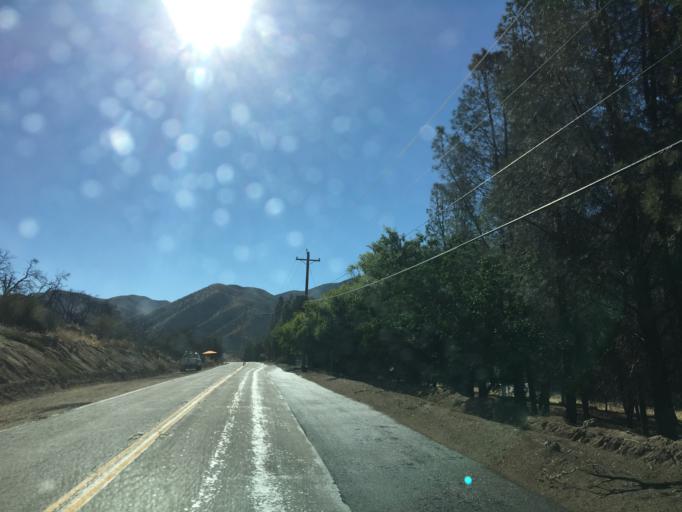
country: US
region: California
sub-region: Los Angeles County
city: Green Valley
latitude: 34.6540
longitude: -118.4758
